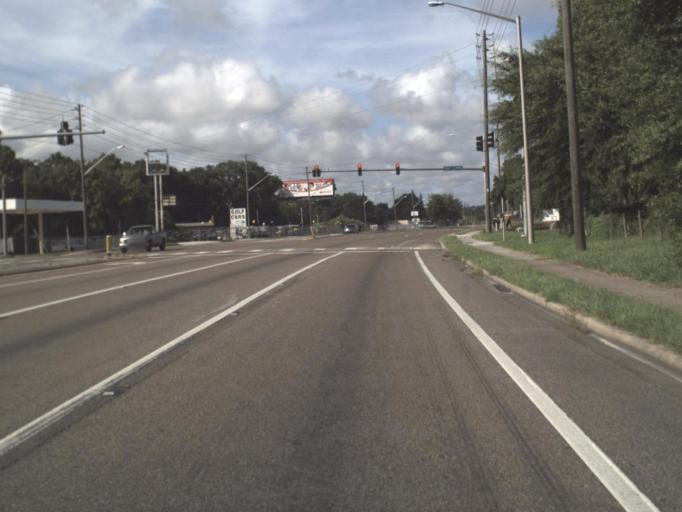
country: US
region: Florida
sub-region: Pasco County
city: Land O' Lakes
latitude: 28.2196
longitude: -82.4581
